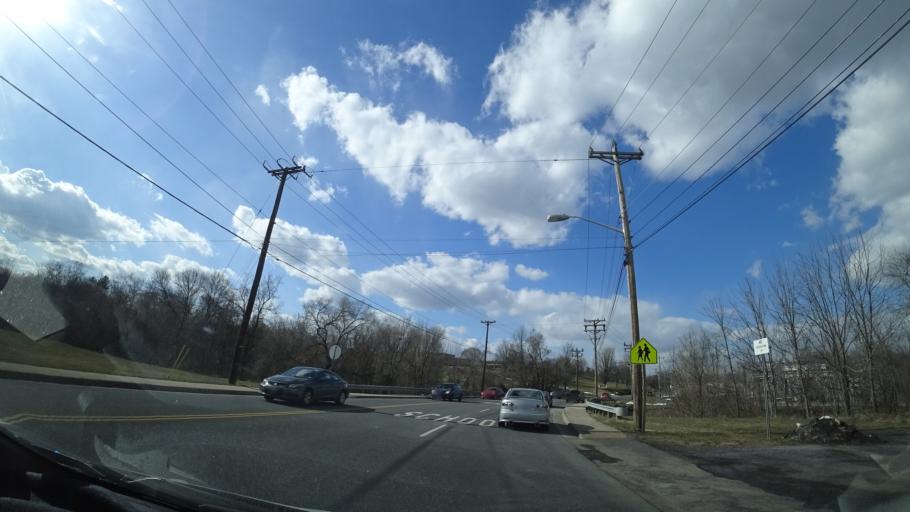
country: US
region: Virginia
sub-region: City of Harrisonburg
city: Harrisonburg
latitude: 38.4368
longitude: -78.8813
